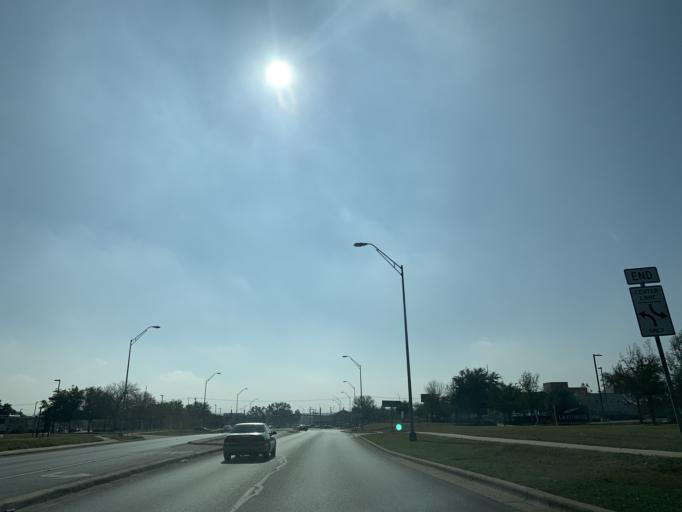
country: US
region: Texas
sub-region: Williamson County
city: Round Rock
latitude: 30.5206
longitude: -97.6557
